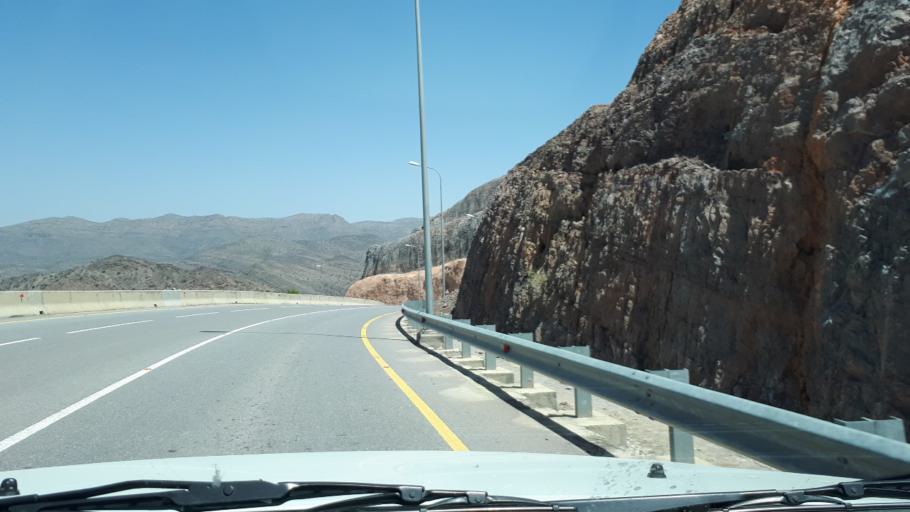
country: OM
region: Muhafazat ad Dakhiliyah
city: Izki
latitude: 23.0596
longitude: 57.7270
